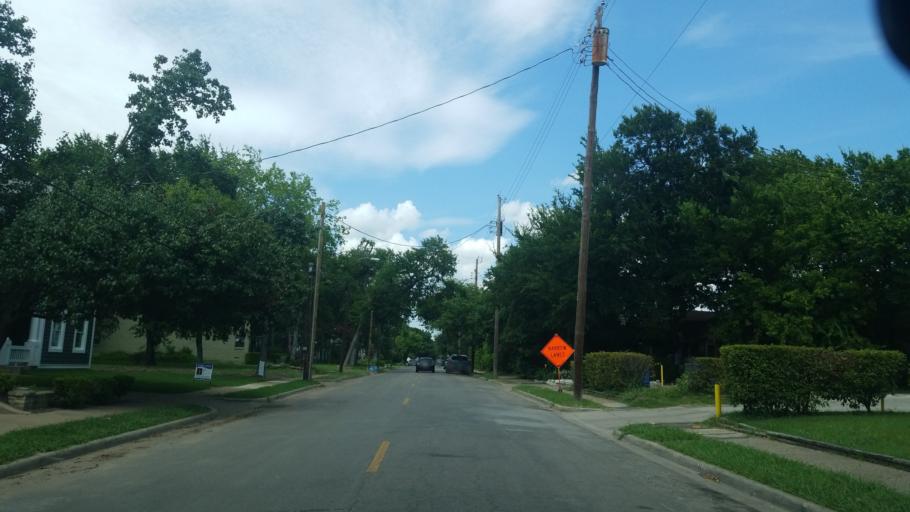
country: US
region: Texas
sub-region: Dallas County
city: Dallas
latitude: 32.7966
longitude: -96.7699
